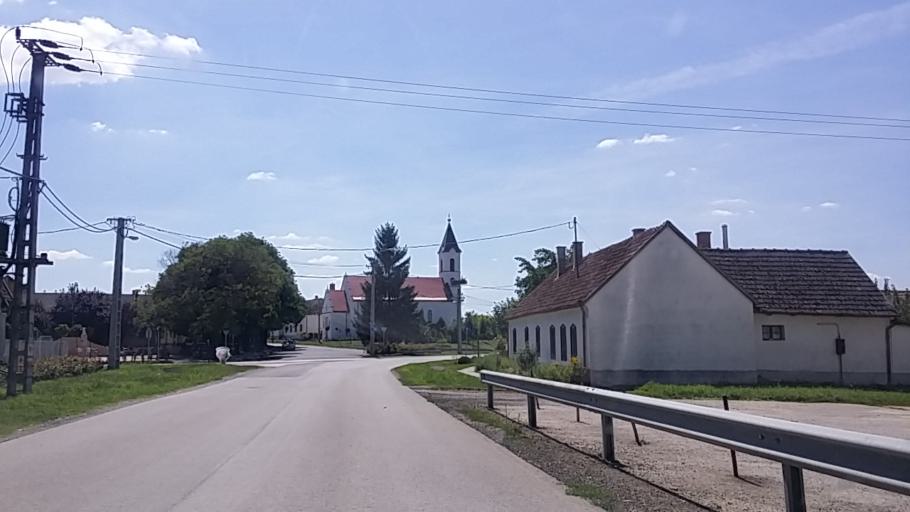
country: HU
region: Fejer
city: Deg
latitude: 46.8702
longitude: 18.4436
